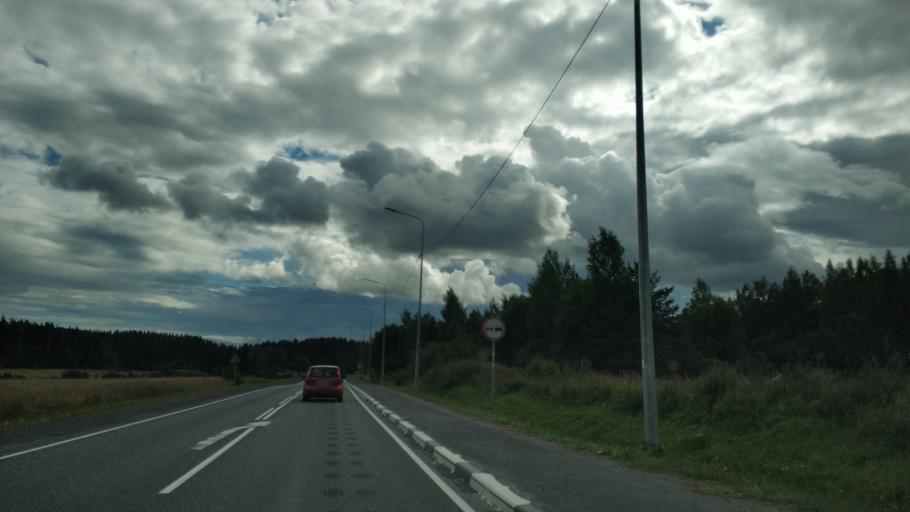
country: RU
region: Republic of Karelia
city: Khelyulya
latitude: 61.7657
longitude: 30.6551
